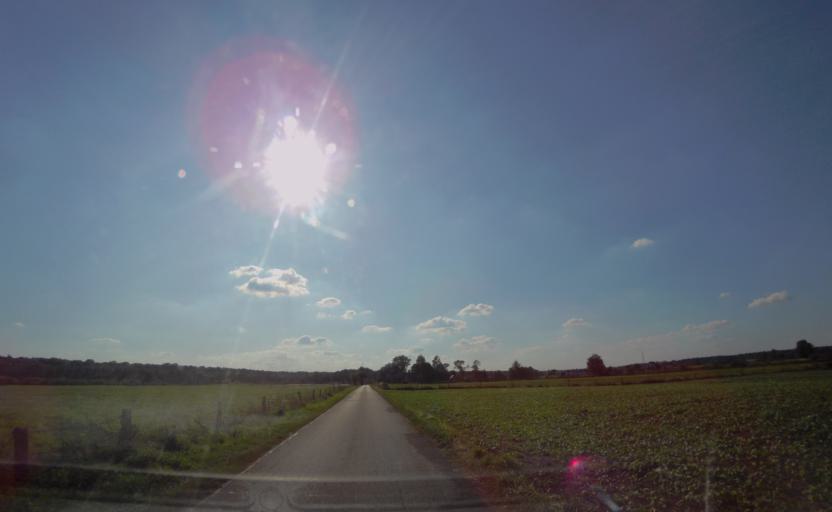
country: PL
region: Subcarpathian Voivodeship
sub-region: Powiat lezajski
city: Stare Miasto
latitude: 50.3000
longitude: 22.3907
